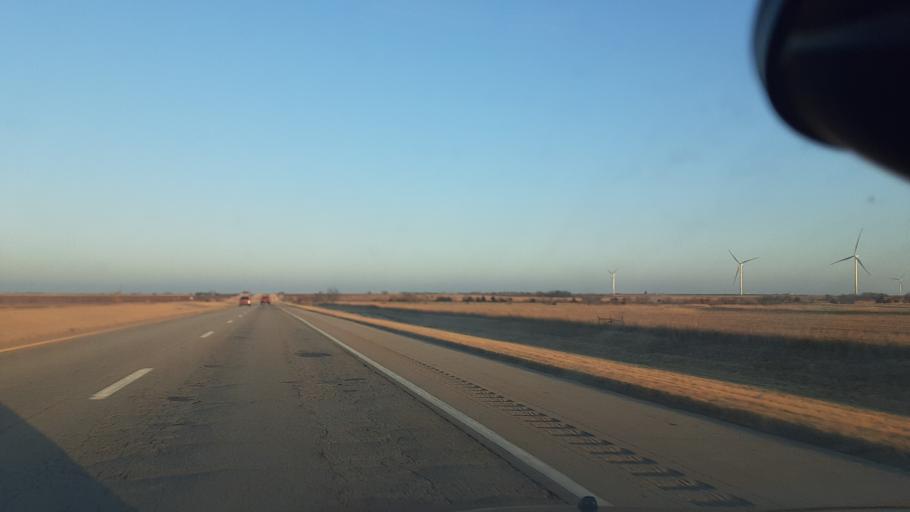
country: US
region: Oklahoma
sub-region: Noble County
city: Perry
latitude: 36.3979
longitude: -97.3945
